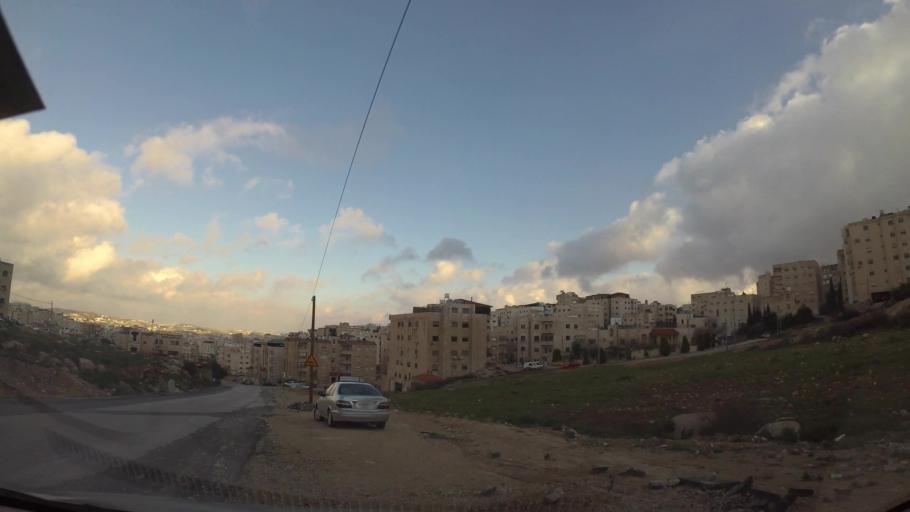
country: JO
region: Amman
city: Al Jubayhah
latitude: 32.0512
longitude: 35.8888
